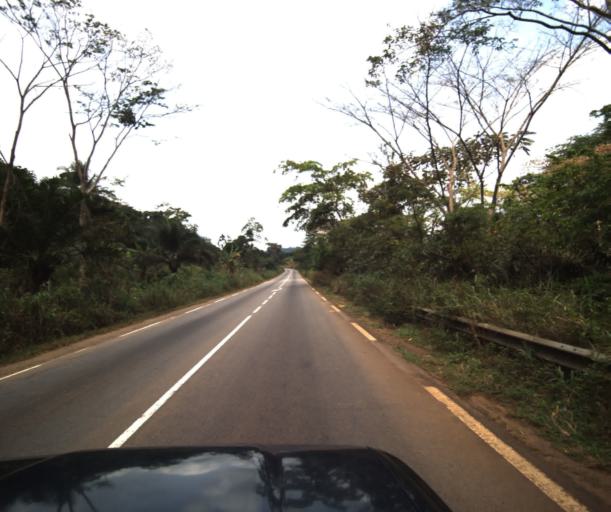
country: CM
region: Centre
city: Mbankomo
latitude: 3.7919
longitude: 11.2994
